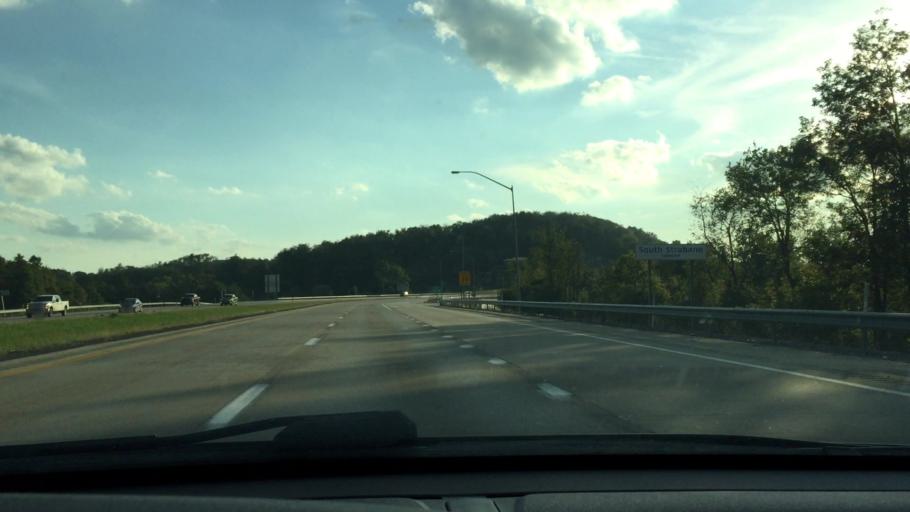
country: US
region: Pennsylvania
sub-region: Washington County
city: McGovern
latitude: 40.2127
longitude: -80.2205
